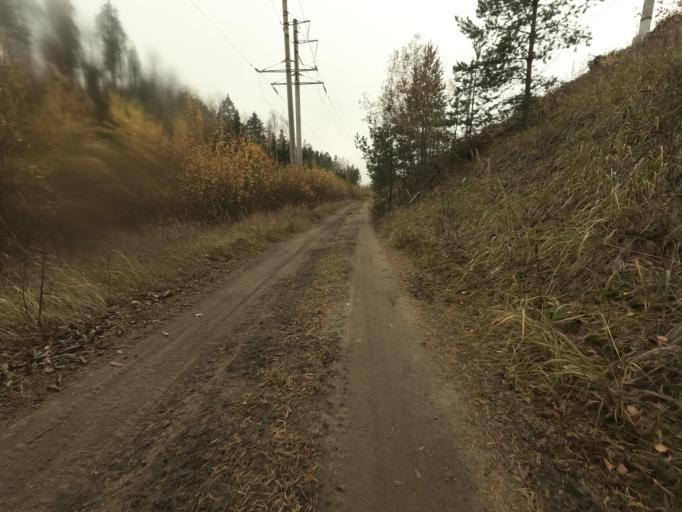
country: RU
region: Leningrad
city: Pavlovo
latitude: 59.7695
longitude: 30.9109
